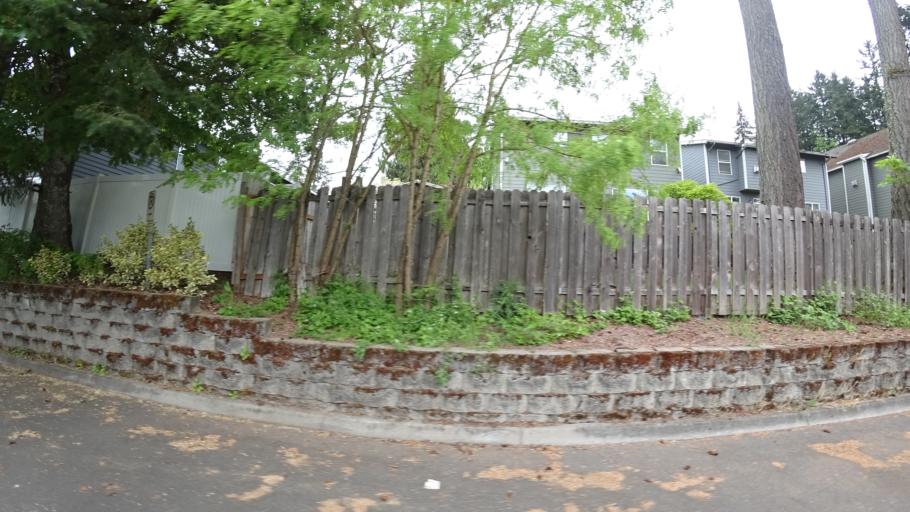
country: US
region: Oregon
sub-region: Washington County
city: Hillsboro
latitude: 45.5191
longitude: -122.9318
